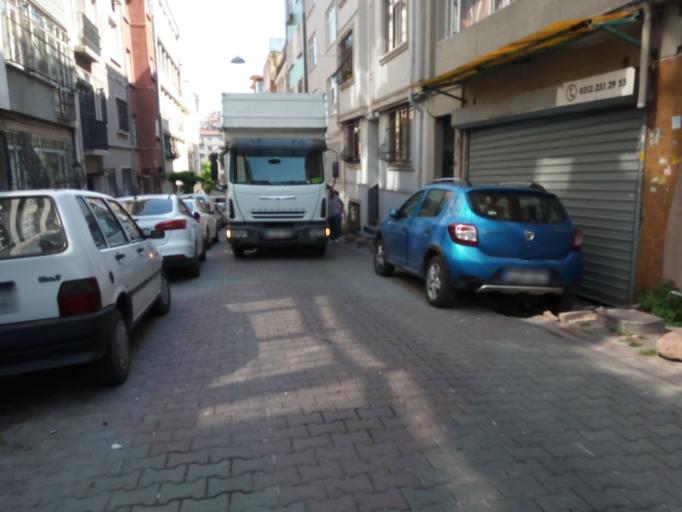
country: TR
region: Istanbul
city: Eminoenue
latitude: 41.0340
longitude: 28.9863
